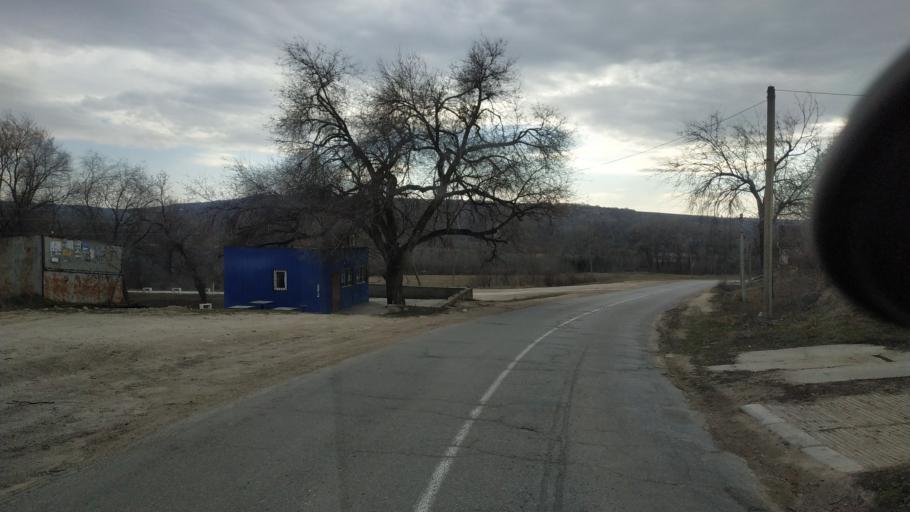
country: MD
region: Chisinau
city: Vadul lui Voda
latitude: 47.1185
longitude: 29.0633
